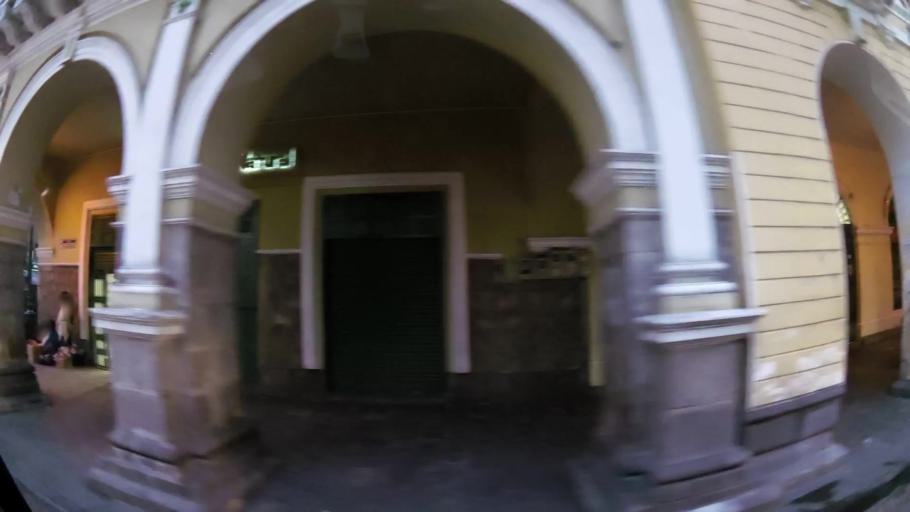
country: EC
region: Tungurahua
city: Ambato
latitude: -1.2422
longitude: -78.6289
